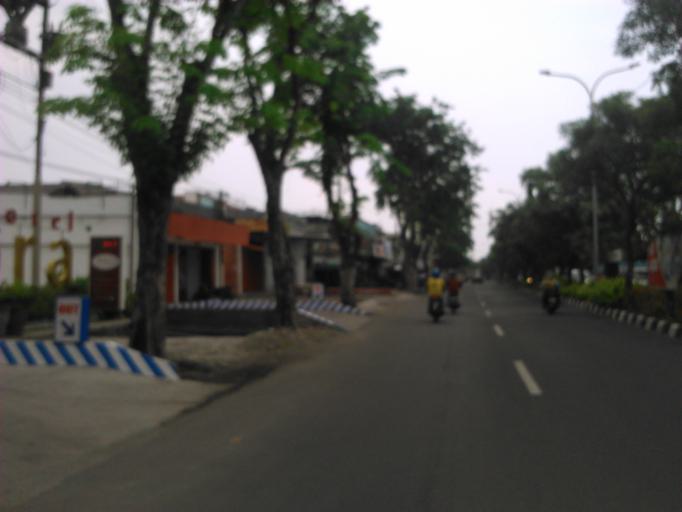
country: ID
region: East Java
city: Gubengairlangga
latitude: -7.2762
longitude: 112.7623
